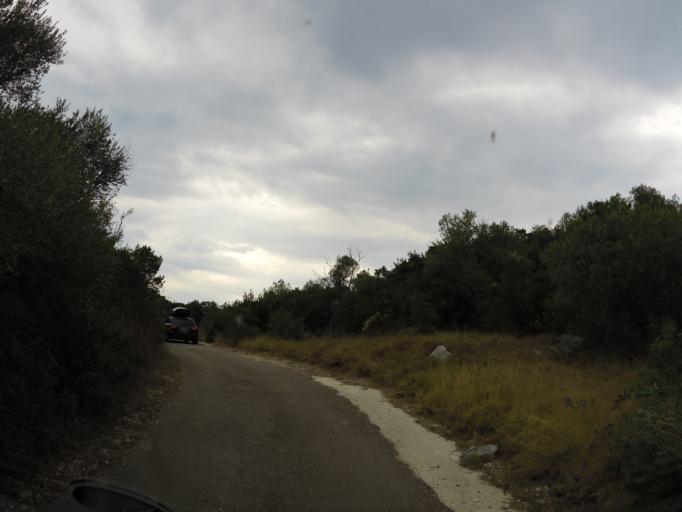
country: HR
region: Zadarska
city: Sali
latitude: 43.9171
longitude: 15.1260
